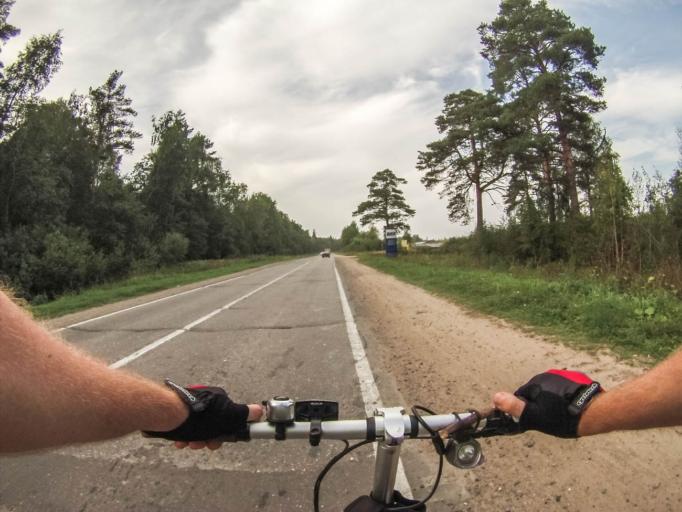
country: RU
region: Jaroslavl
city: Uglich
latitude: 57.4905
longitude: 38.3542
